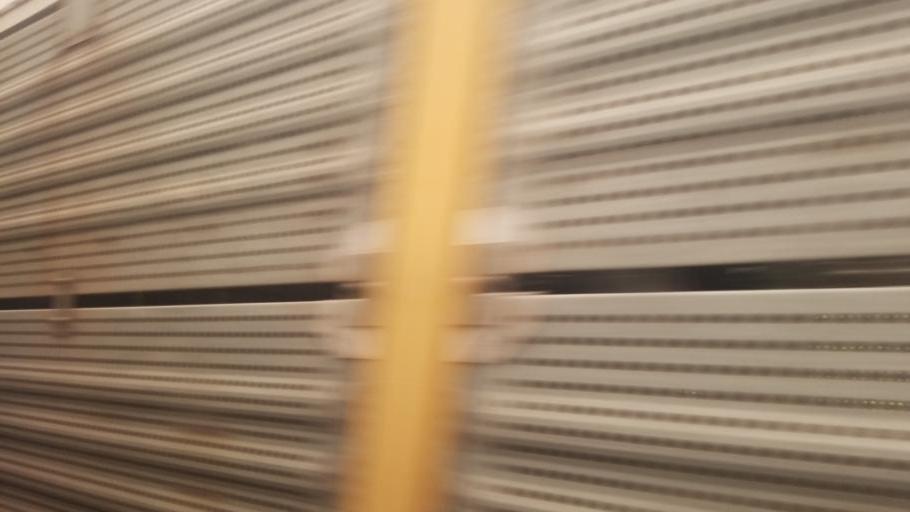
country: US
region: Pennsylvania
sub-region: Somerset County
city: Milford
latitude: 39.8779
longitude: -79.0907
